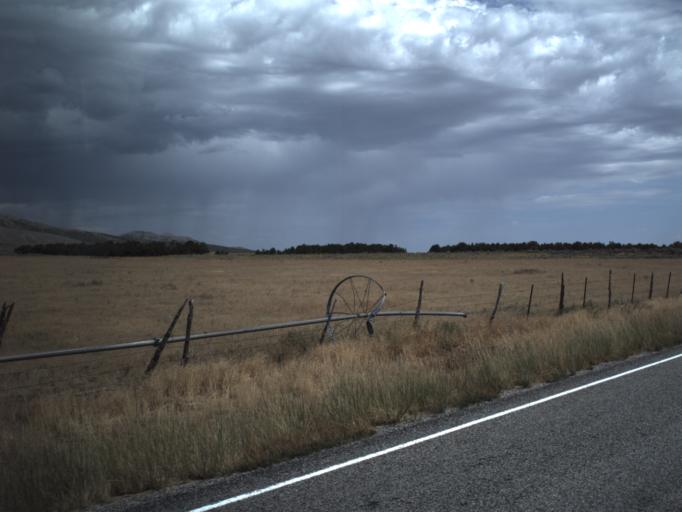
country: US
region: Idaho
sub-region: Cassia County
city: Burley
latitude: 41.8171
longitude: -113.3061
